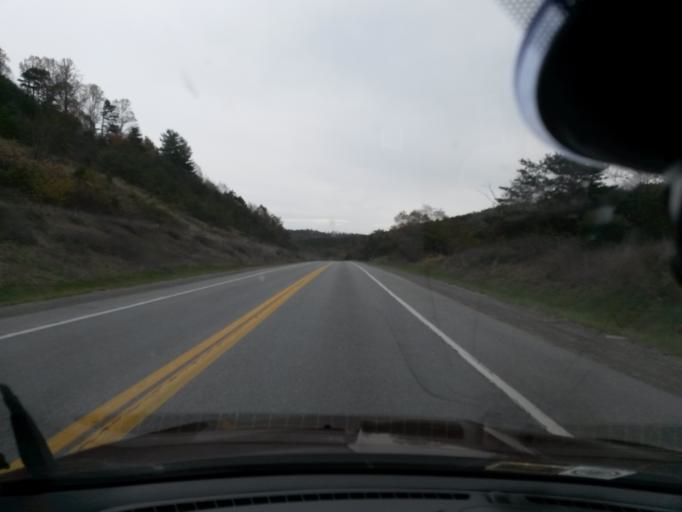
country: US
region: Virginia
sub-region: Alleghany County
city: Clifton Forge
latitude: 37.7630
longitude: -79.7859
